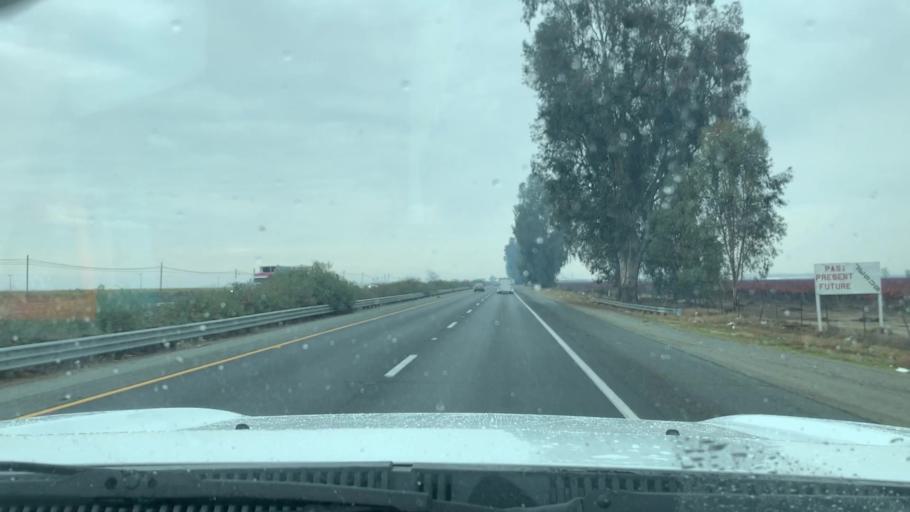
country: US
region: California
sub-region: Kern County
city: Delano
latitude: 35.8054
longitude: -119.2558
